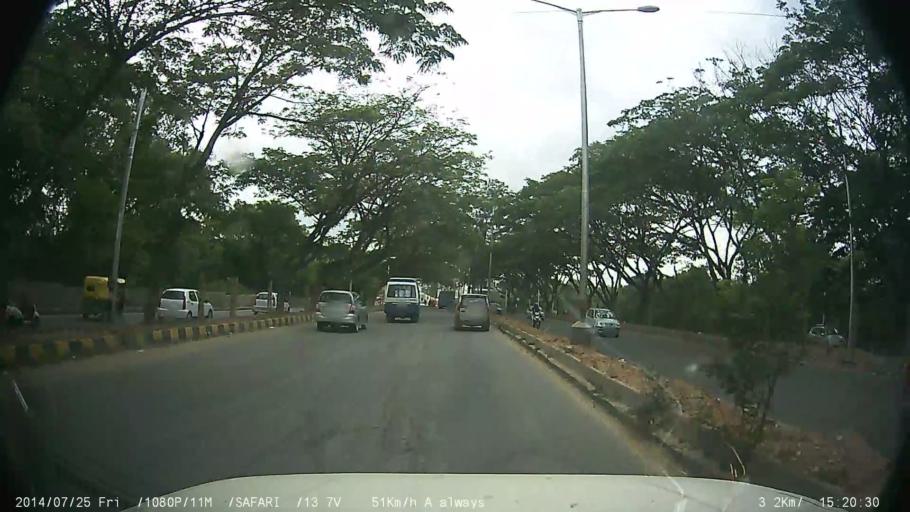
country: IN
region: Karnataka
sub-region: Bangalore Urban
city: Bangalore
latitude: 12.9231
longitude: 77.6568
